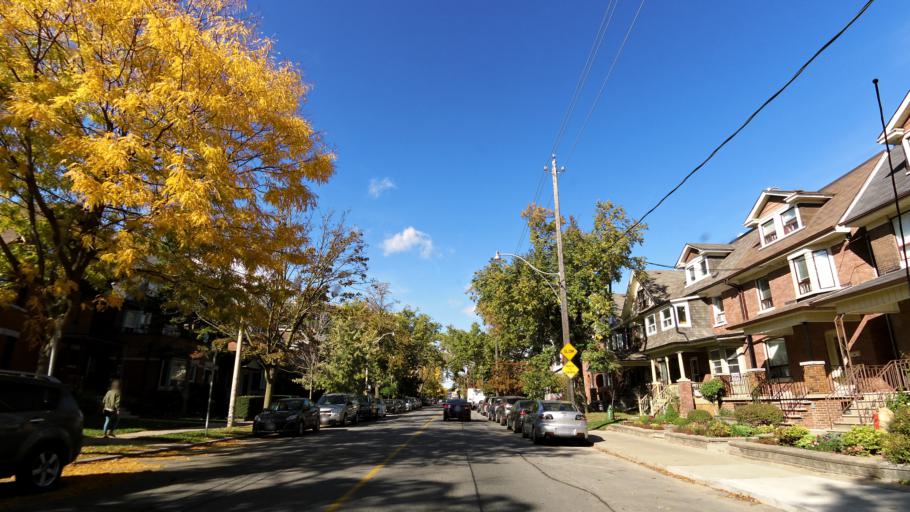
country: CA
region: Ontario
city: Toronto
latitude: 43.6571
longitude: -79.4277
